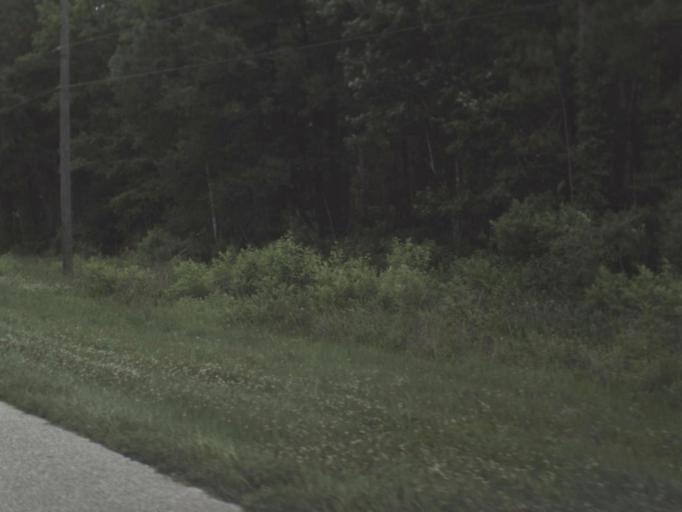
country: US
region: Florida
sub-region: Saint Johns County
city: Palm Valley
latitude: 30.0619
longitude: -81.4364
